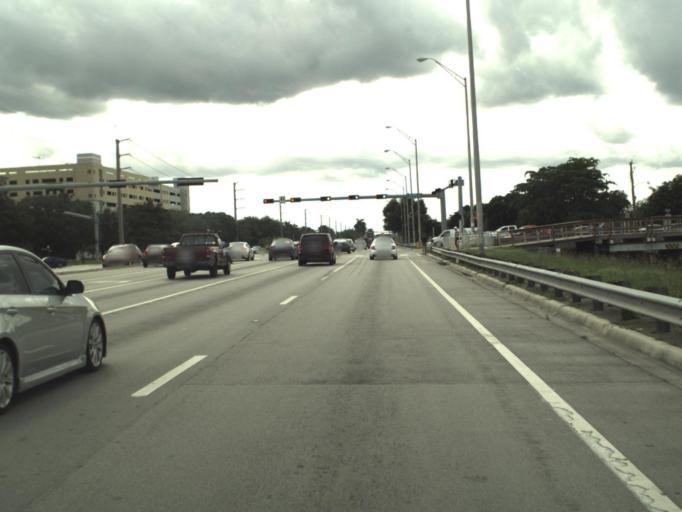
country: US
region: Florida
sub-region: Miami-Dade County
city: Sweetwater
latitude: 25.7614
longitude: -80.3714
